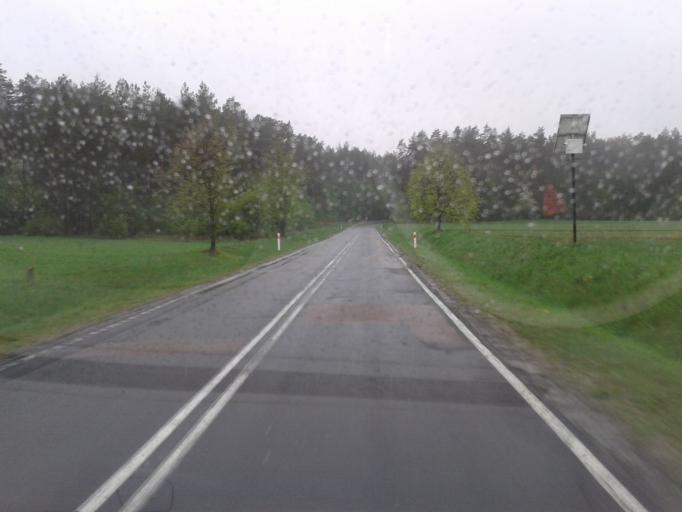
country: PL
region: Subcarpathian Voivodeship
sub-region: Powiat lubaczowski
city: Narol
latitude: 50.3209
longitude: 23.2702
